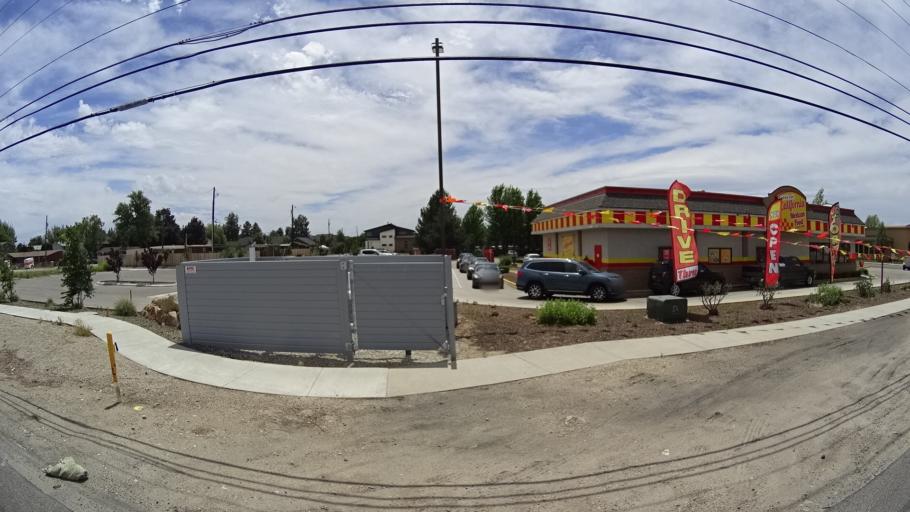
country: US
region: Idaho
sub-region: Ada County
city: Meridian
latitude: 43.6194
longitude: -116.3177
